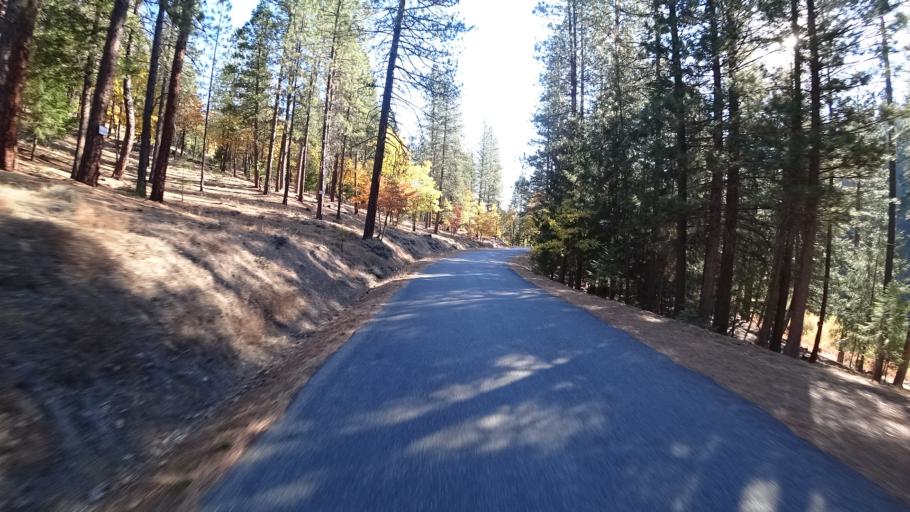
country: US
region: California
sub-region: Siskiyou County
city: Yreka
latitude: 41.6408
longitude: -123.0051
